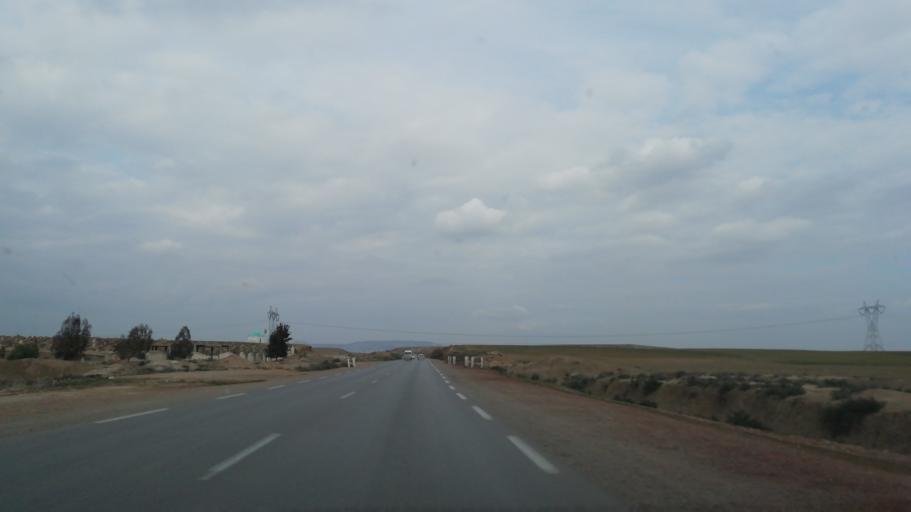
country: DZ
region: Mostaganem
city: Mostaganem
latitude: 35.7094
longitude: 0.0545
